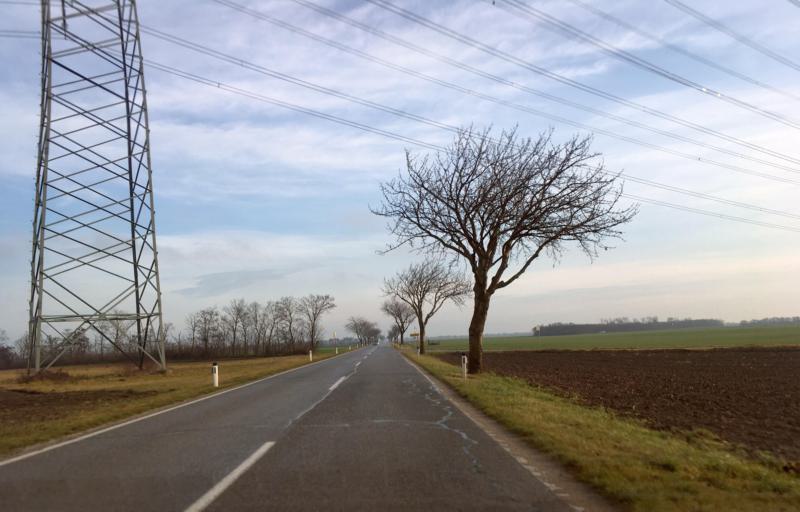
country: AT
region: Lower Austria
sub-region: Politischer Bezirk Ganserndorf
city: Gross-Enzersdorf
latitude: 48.2093
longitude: 16.5786
